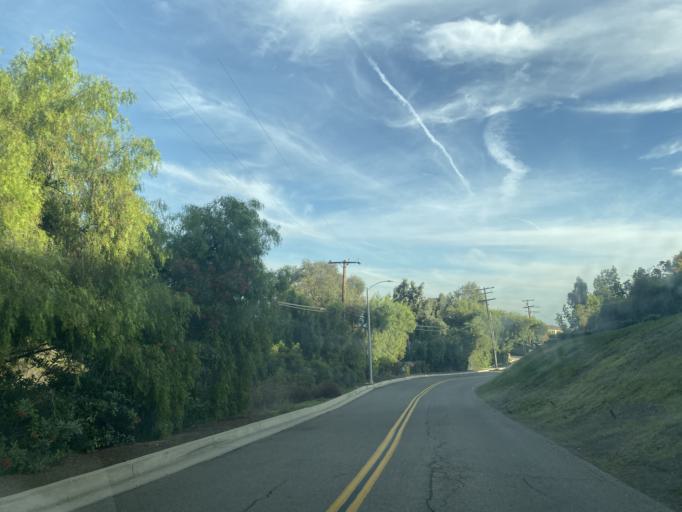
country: US
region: California
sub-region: Orange County
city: Brea
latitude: 33.8903
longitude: -117.9000
